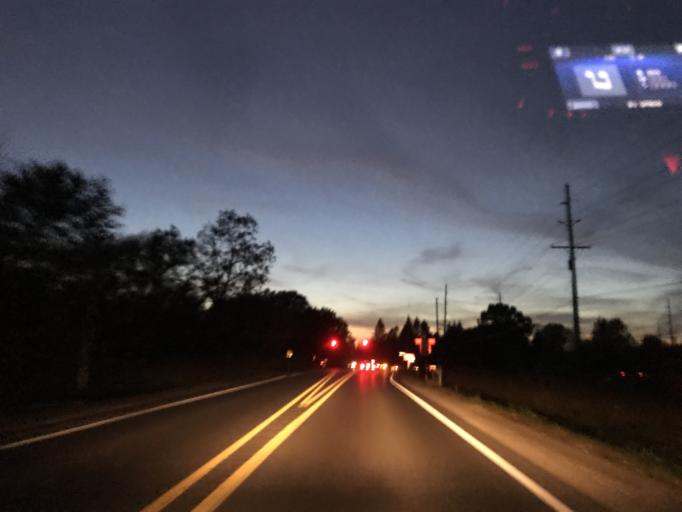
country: US
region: Michigan
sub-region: Oakland County
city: South Lyon
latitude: 42.4325
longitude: -83.6279
